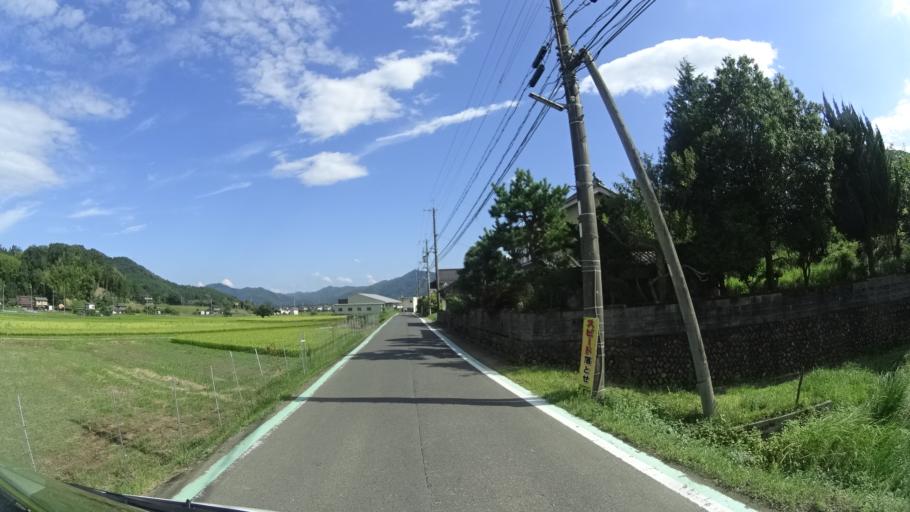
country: JP
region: Kyoto
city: Fukuchiyama
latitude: 35.3223
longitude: 135.1801
